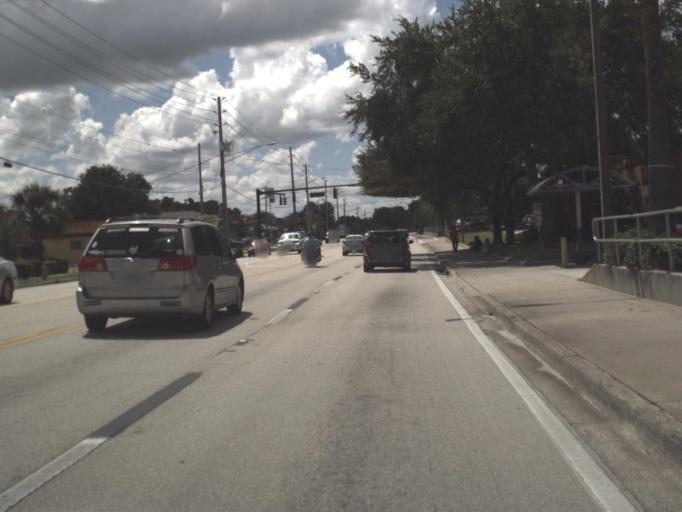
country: US
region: Florida
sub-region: Polk County
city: Lakeland
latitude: 28.0609
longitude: -81.9533
